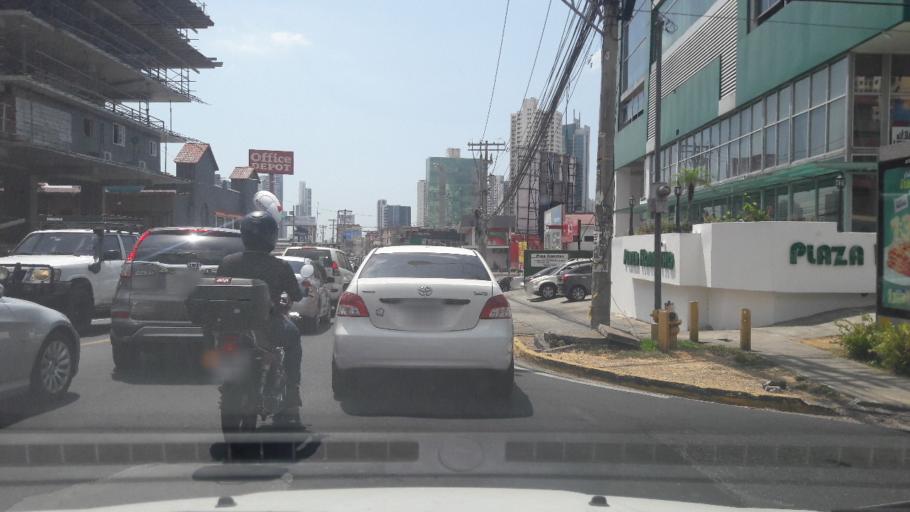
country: PA
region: Panama
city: Panama
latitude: 8.9920
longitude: -79.5220
